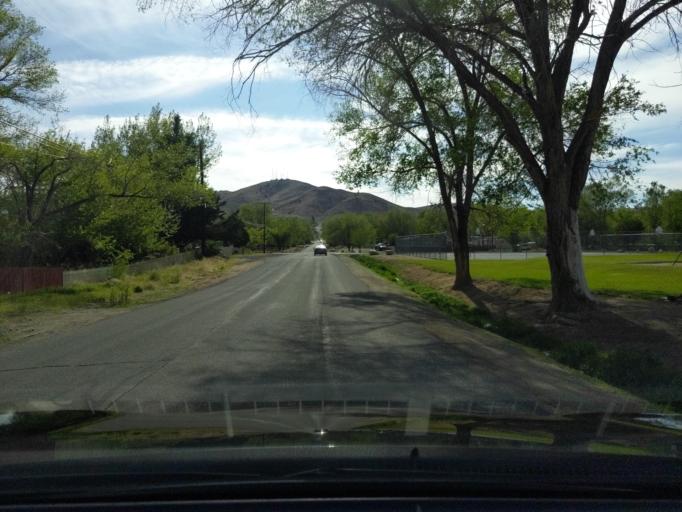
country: US
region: Nevada
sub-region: Washoe County
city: Sun Valley
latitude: 39.5855
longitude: -119.7744
